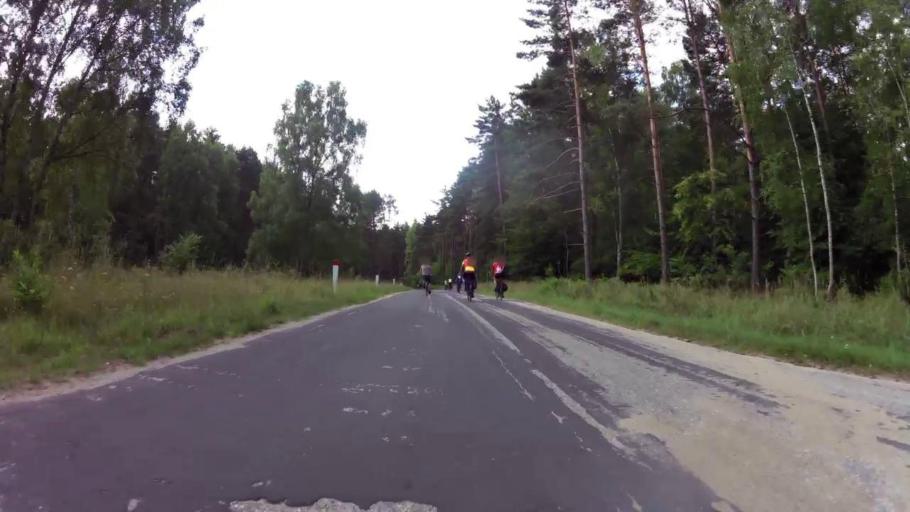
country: PL
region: West Pomeranian Voivodeship
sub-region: Powiat drawski
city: Drawsko Pomorskie
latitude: 53.4643
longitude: 15.7773
